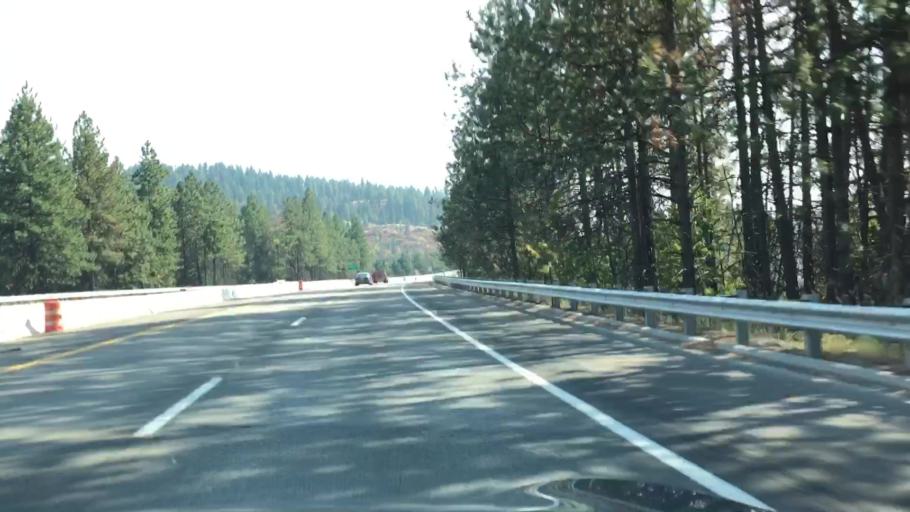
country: US
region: Idaho
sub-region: Kootenai County
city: Coeur d'Alene
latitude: 47.6747
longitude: -116.7518
